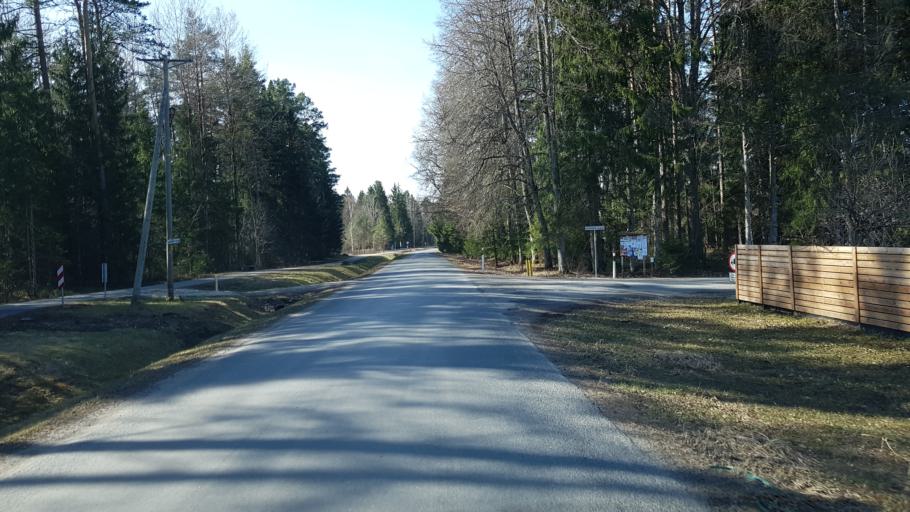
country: EE
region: Harju
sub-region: Saku vald
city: Saku
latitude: 59.2611
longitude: 24.6585
